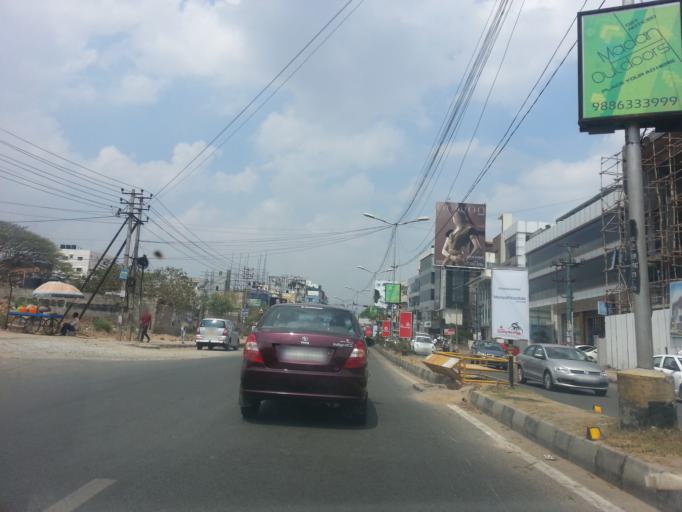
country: IN
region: Karnataka
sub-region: Bangalore Urban
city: Bangalore
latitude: 12.9560
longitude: 77.6414
